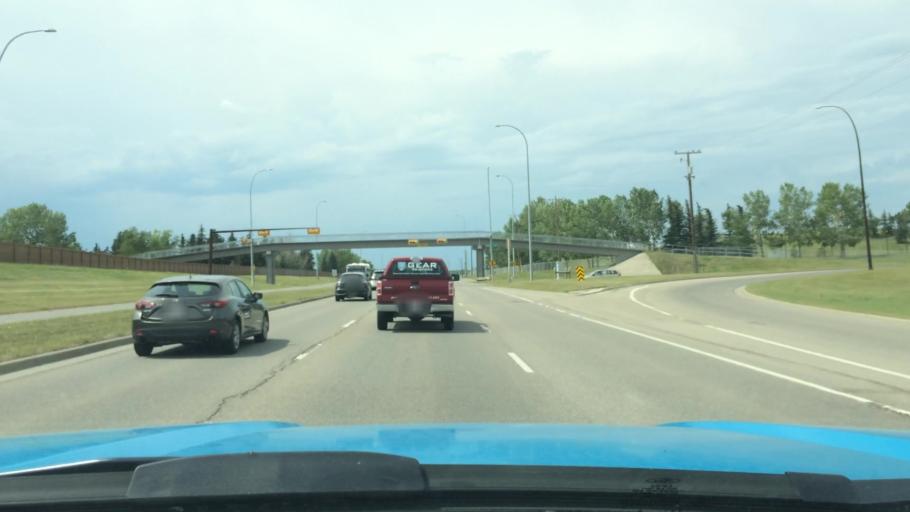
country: CA
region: Alberta
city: Calgary
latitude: 51.1121
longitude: -114.1467
